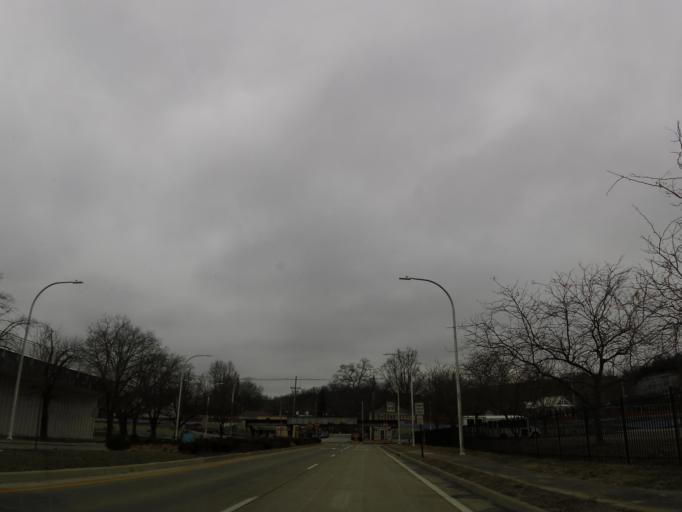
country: US
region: Kentucky
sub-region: Franklin County
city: Frankfort
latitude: 38.2019
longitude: -84.8794
